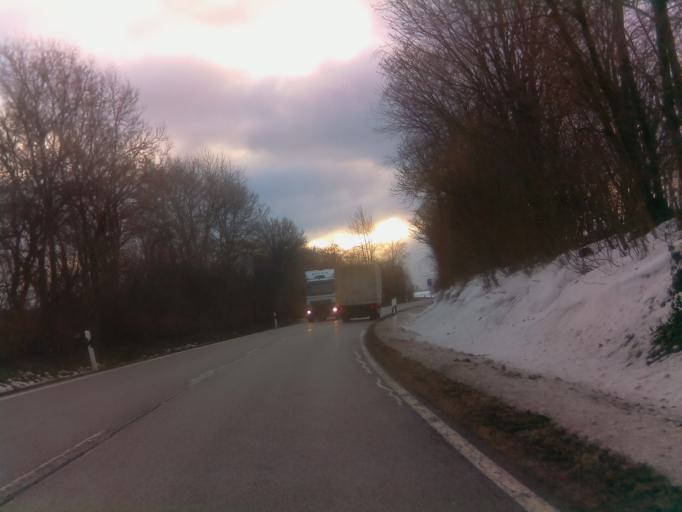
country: DE
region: Baden-Wuerttemberg
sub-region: Karlsruhe Region
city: Zwingenberg
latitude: 49.4636
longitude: 9.0909
